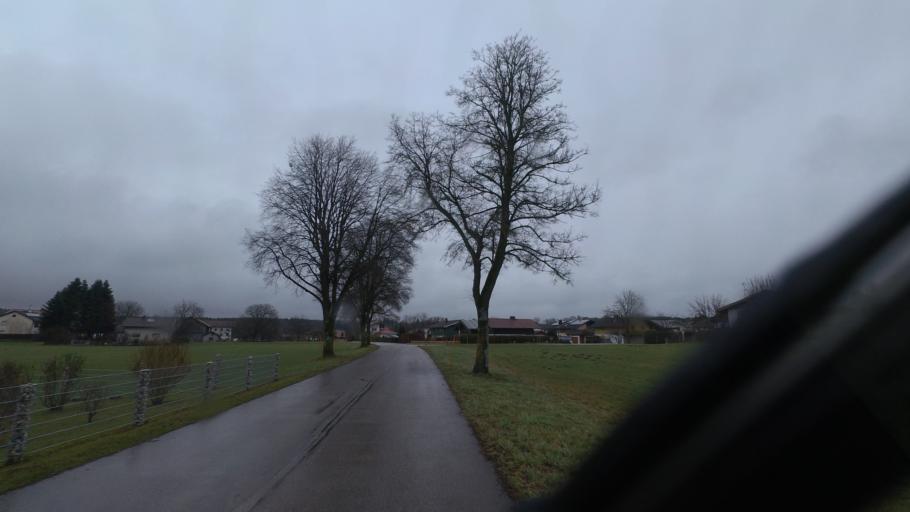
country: DE
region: Bavaria
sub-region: Upper Bavaria
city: Nussdorf
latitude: 47.9083
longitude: 12.6148
